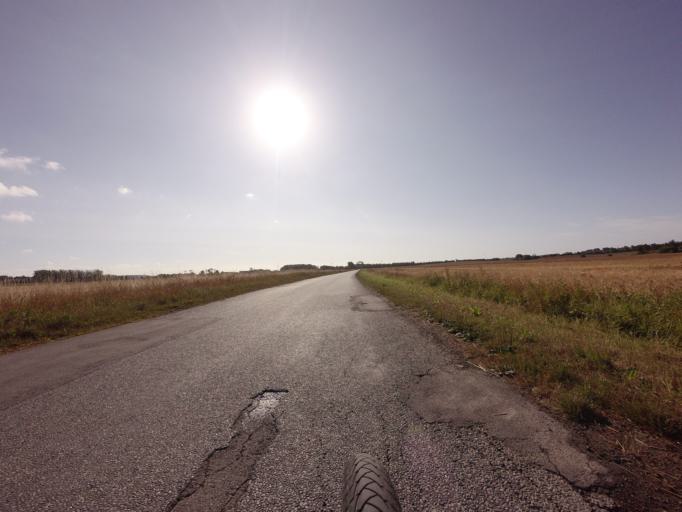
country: DK
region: North Denmark
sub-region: Hjorring Kommune
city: Vra
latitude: 57.3912
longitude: 9.9743
